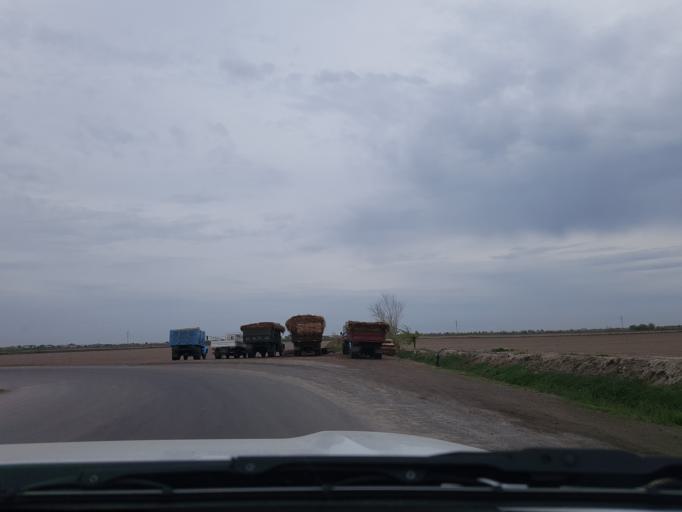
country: TM
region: Lebap
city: Turkmenabat
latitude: 39.0721
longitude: 63.5654
